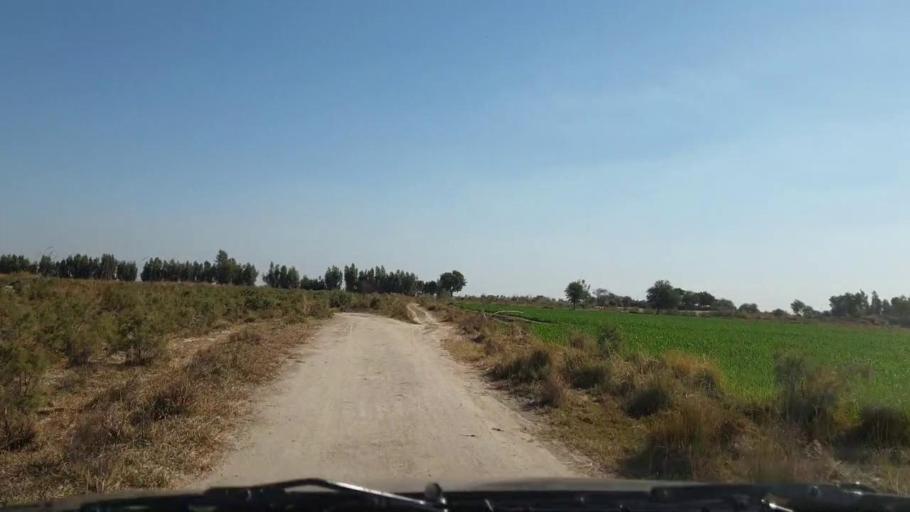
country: PK
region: Sindh
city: Sinjhoro
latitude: 26.1338
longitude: 68.8454
